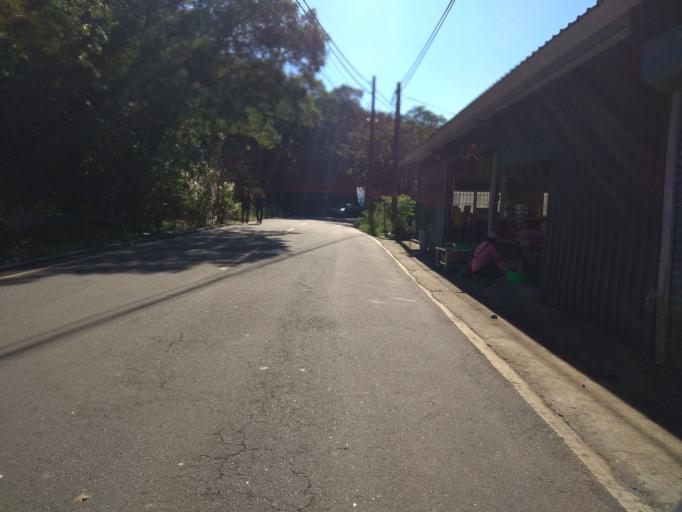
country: TW
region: Taiwan
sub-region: Hsinchu
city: Zhubei
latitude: 24.8604
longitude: 121.1044
